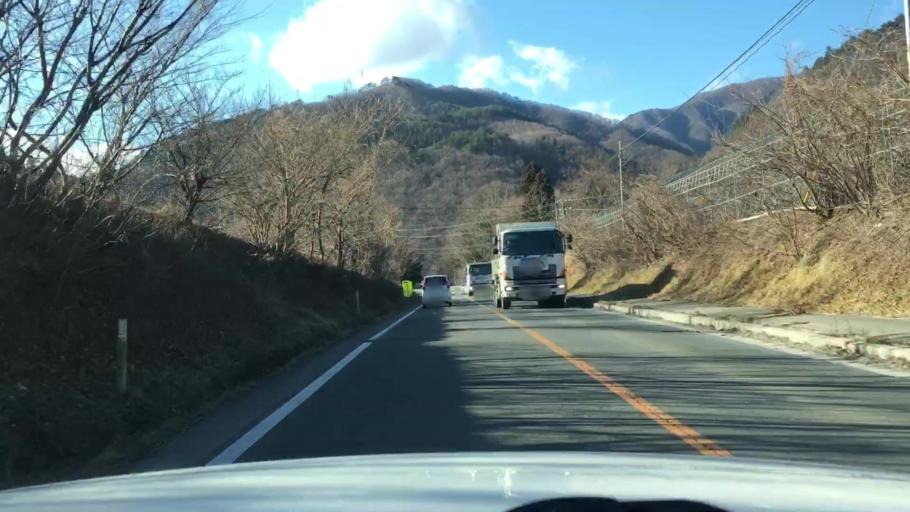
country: JP
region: Iwate
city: Miyako
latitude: 39.6027
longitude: 141.7705
